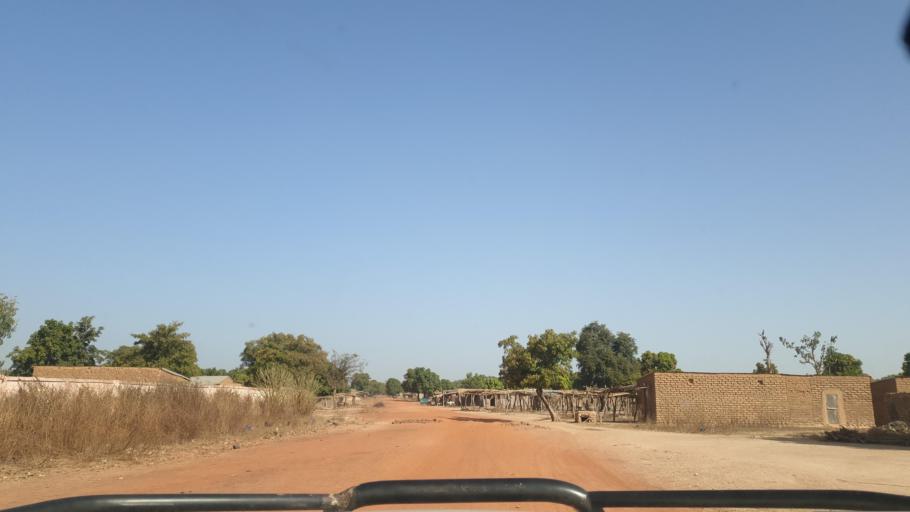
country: ML
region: Sikasso
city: Kolondieba
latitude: 11.7653
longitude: -6.9021
